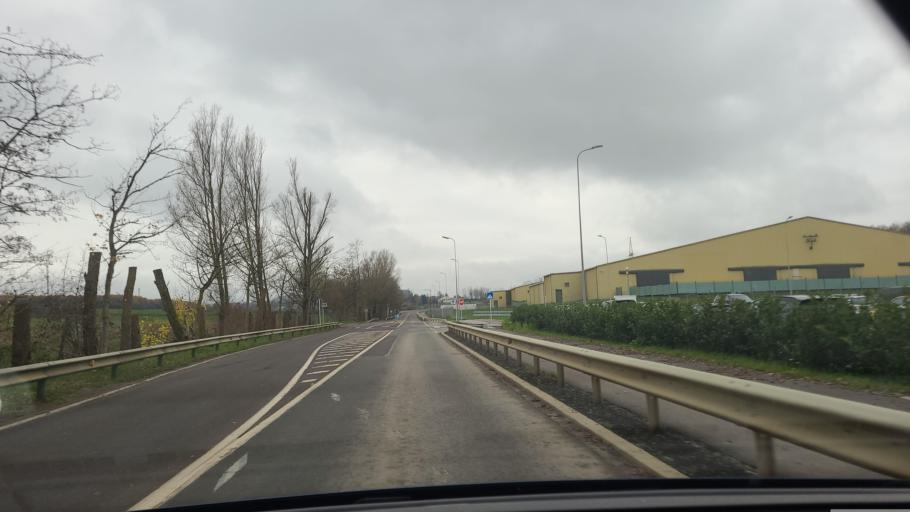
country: LU
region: Luxembourg
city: Soleuvre
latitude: 49.5411
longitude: 5.9549
